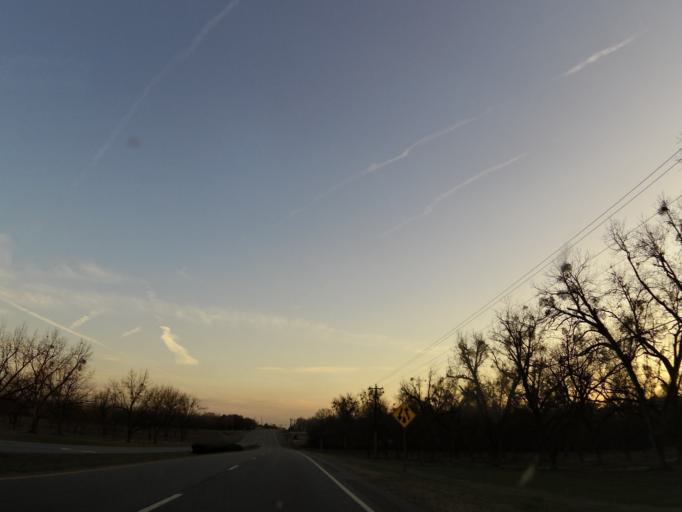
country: US
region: Georgia
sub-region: Lee County
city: Leesburg
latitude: 31.6855
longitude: -84.1729
